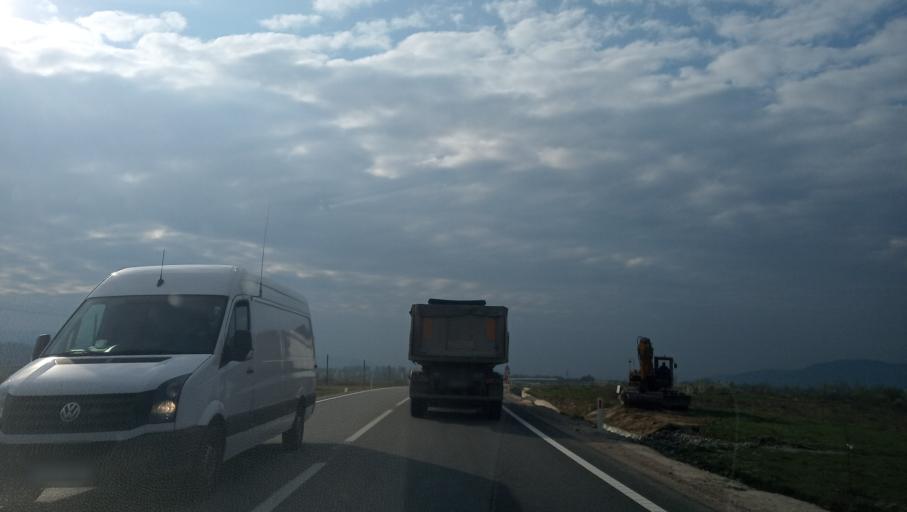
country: RO
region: Bihor
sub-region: Comuna Rieni
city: Rieni
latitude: 46.5692
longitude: 22.4424
